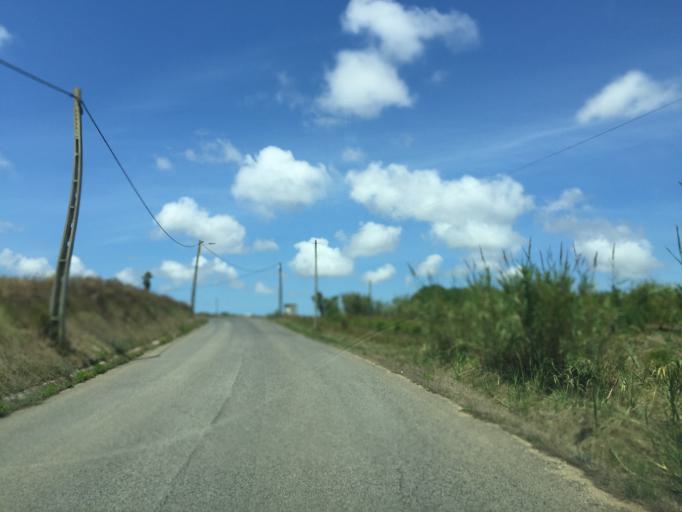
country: PT
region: Leiria
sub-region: Bombarral
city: Bombarral
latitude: 39.2809
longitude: -9.2304
